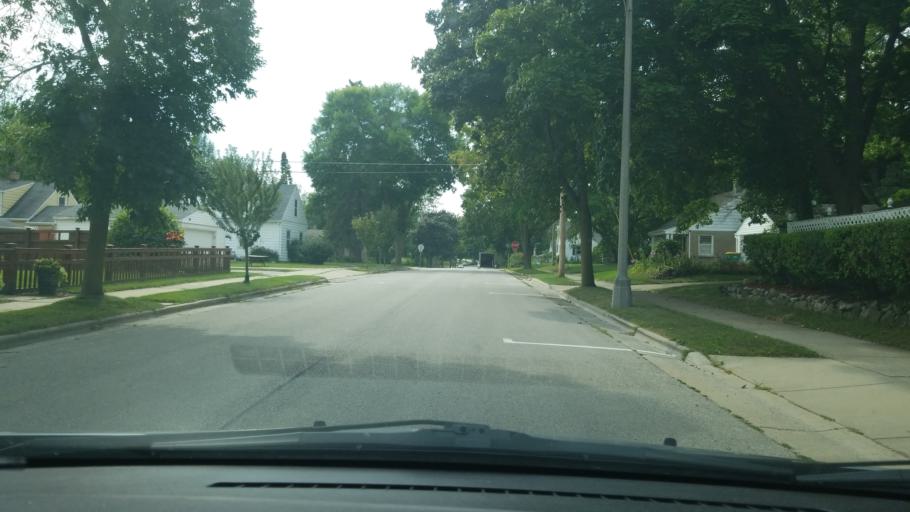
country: US
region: Wisconsin
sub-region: Ozaukee County
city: Cedarburg
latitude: 43.3036
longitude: -87.9914
